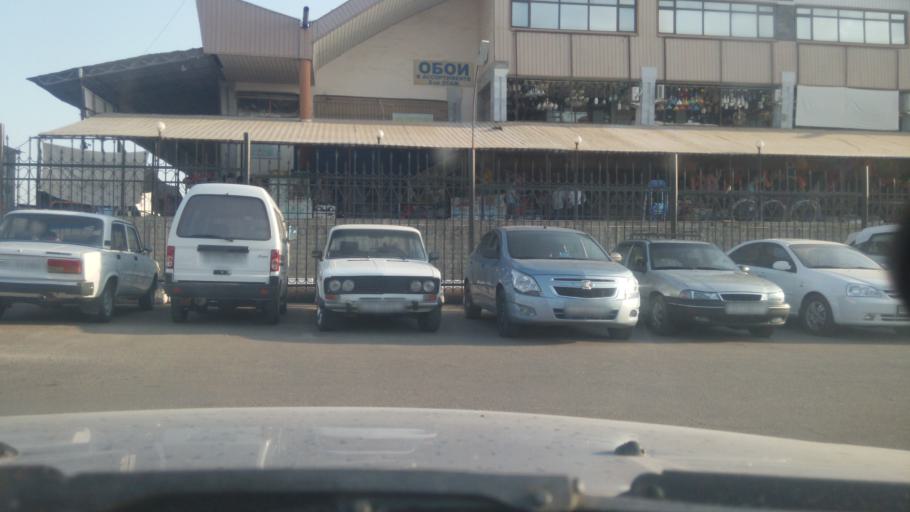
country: UZ
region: Toshkent Shahri
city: Tashkent
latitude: 41.2872
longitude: 69.1503
